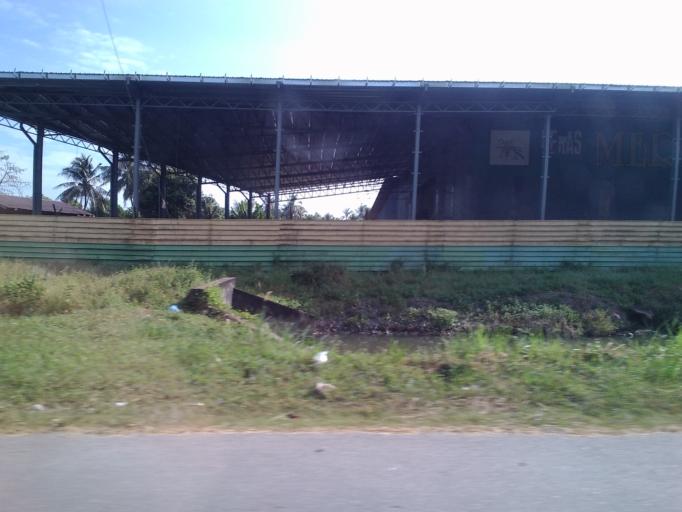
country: MY
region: Kedah
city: Gurun
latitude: 5.9601
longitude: 100.4052
